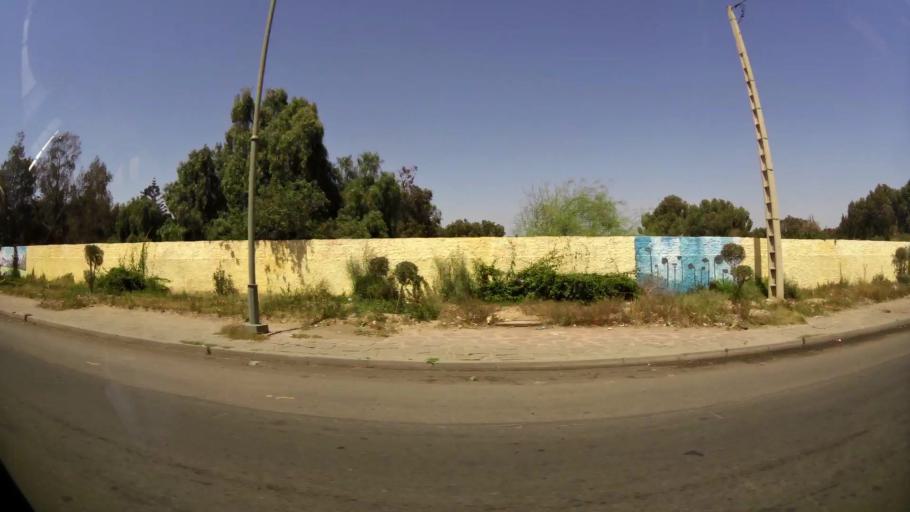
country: MA
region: Souss-Massa-Draa
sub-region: Inezgane-Ait Mellou
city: Inezgane
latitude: 30.3538
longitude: -9.5096
